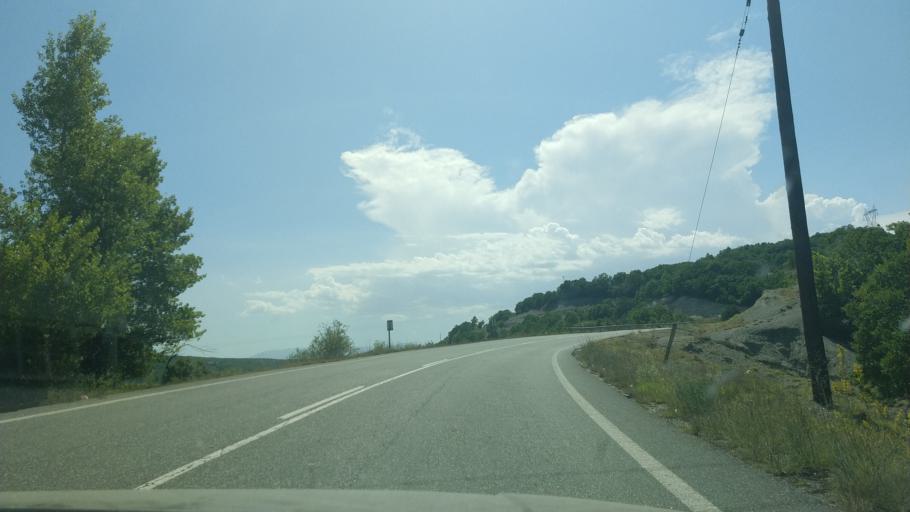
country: GR
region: West Macedonia
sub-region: Nomos Grevenon
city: Grevena
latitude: 40.0507
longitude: 21.4771
